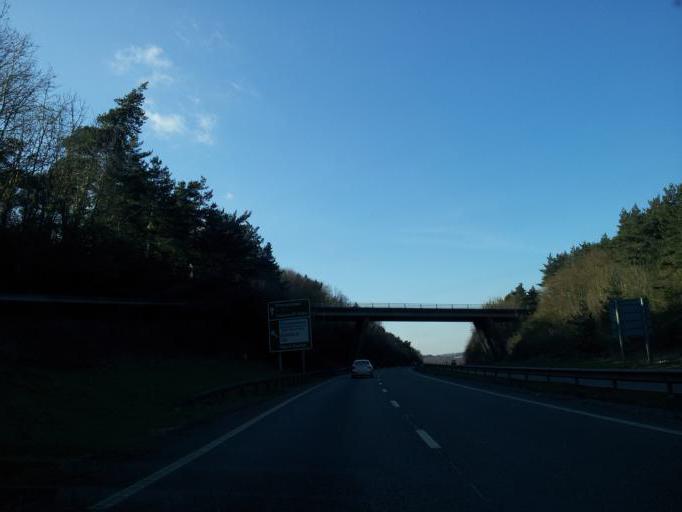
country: GB
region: England
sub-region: Devon
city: Exeter
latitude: 50.6920
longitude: -3.5384
